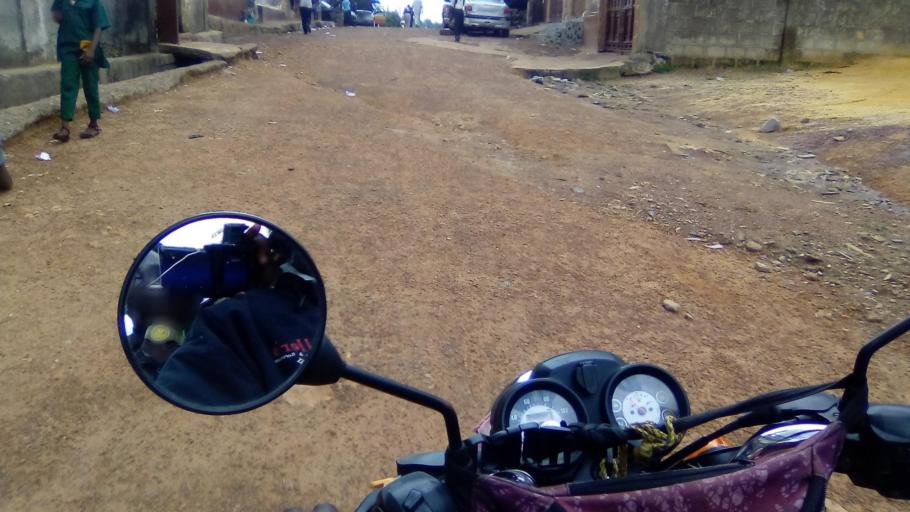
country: SL
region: Southern Province
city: Bo
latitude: 7.9615
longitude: -11.7315
